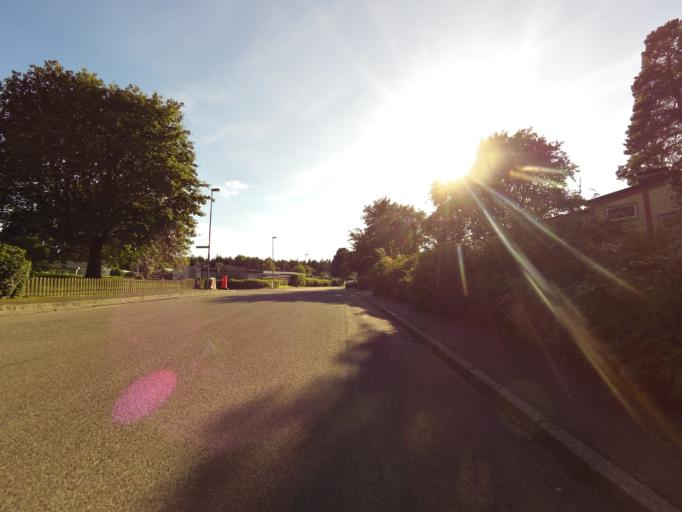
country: SE
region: Gaevleborg
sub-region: Gavle Kommun
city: Gavle
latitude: 60.6582
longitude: 17.1481
